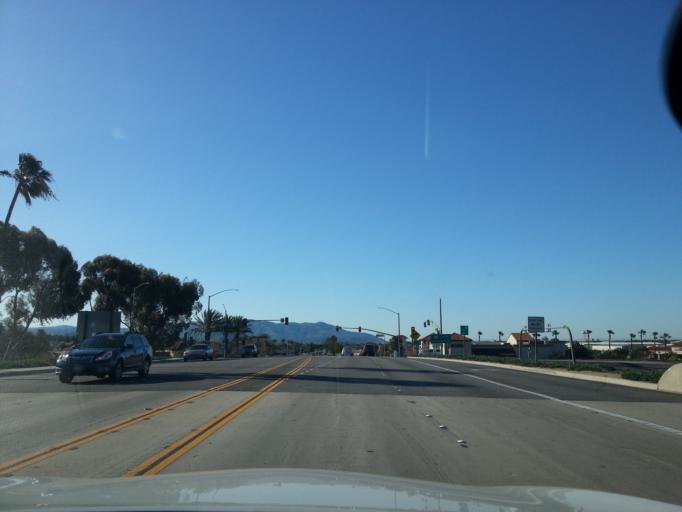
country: US
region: California
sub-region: Ventura County
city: Camarillo
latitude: 34.2190
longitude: -119.0698
